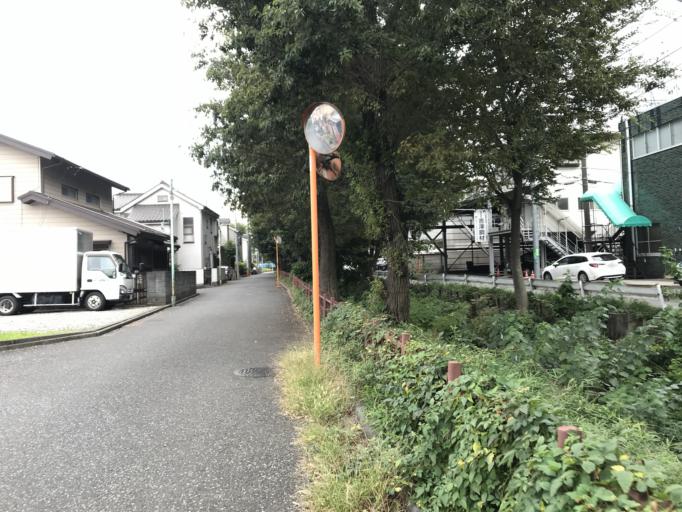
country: JP
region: Tokyo
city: Higashimurayama-shi
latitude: 35.7561
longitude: 139.4894
